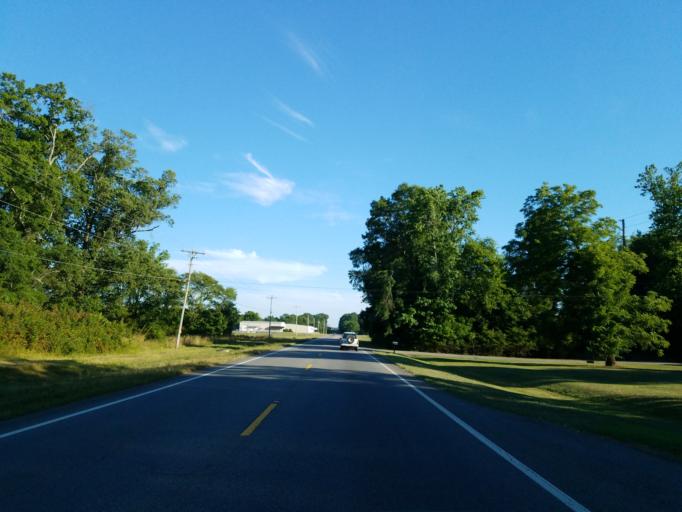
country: US
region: Georgia
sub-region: Gordon County
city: Calhoun
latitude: 34.4411
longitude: -84.9357
